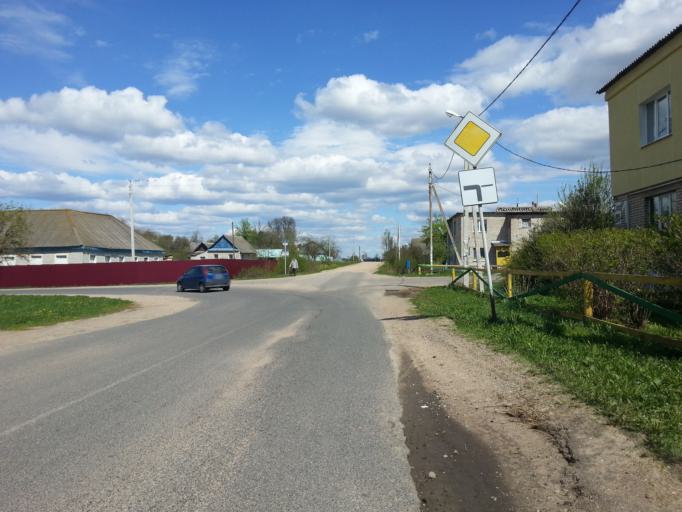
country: BY
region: Minsk
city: Slabada
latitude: 54.0475
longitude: 27.8753
